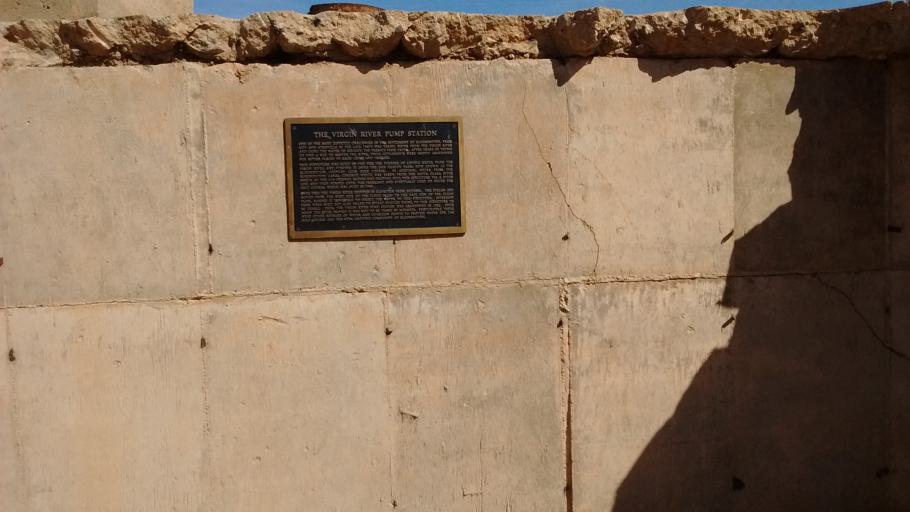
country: US
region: Utah
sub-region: Washington County
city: Saint George
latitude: 37.0544
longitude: -113.6016
